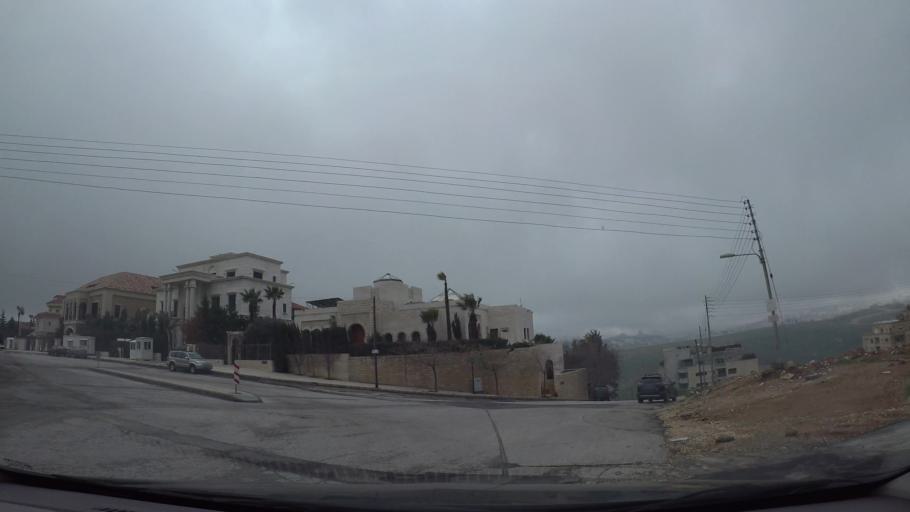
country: JO
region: Amman
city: Al Bunayyat ash Shamaliyah
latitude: 31.9382
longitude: 35.8761
